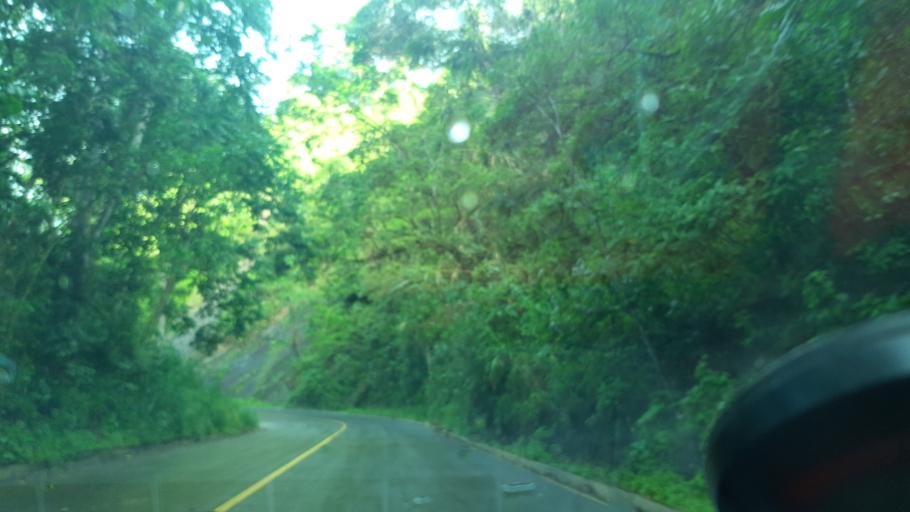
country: CO
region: Cundinamarca
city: Tenza
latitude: 5.0738
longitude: -73.4083
